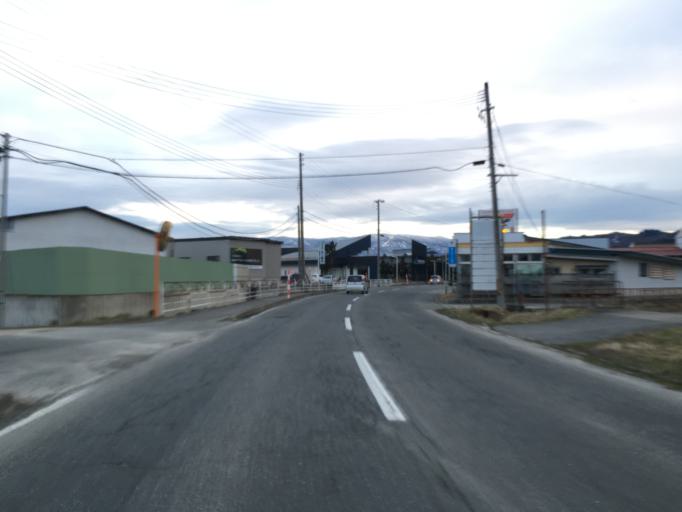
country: JP
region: Yamagata
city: Yonezawa
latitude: 37.9334
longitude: 140.0811
